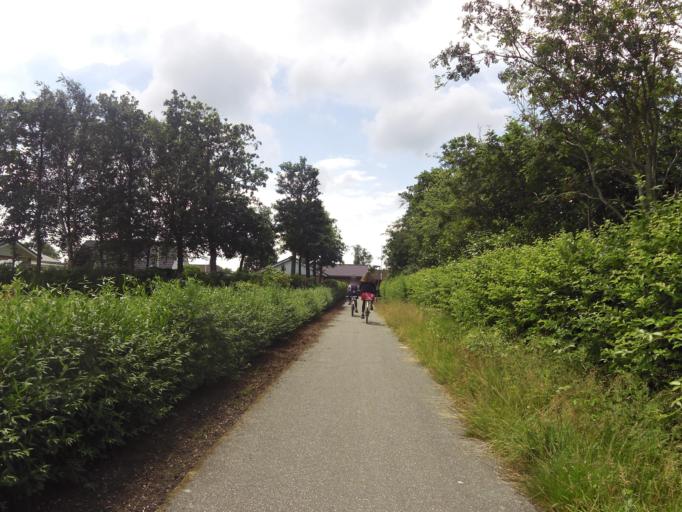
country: DK
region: South Denmark
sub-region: Tonder Kommune
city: Sherrebek
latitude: 55.1548
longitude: 8.7569
